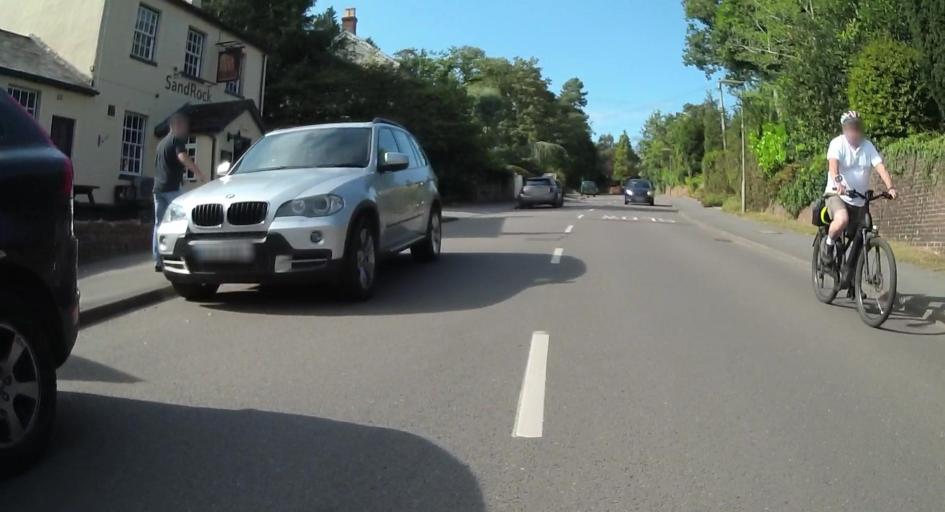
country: GB
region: England
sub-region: Surrey
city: Farnham
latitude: 51.1929
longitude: -0.8129
